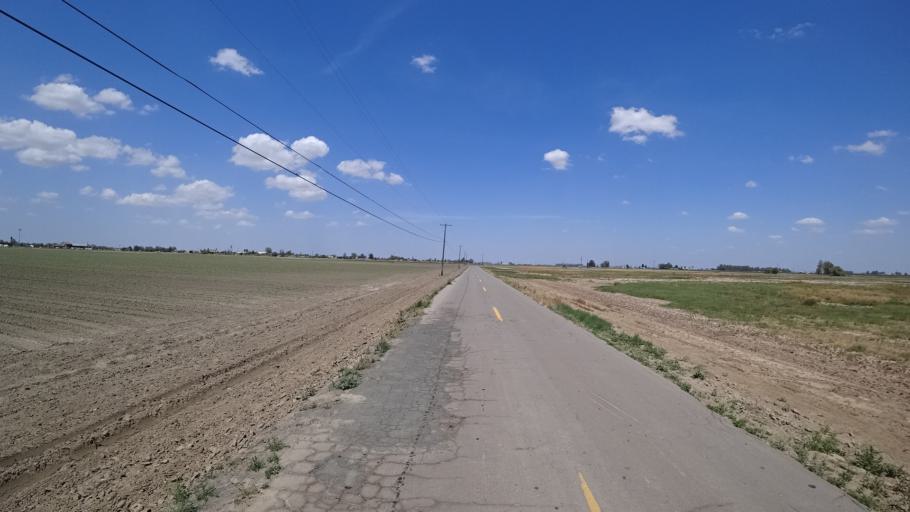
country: US
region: California
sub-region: Kings County
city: Stratford
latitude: 36.1788
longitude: -119.8161
